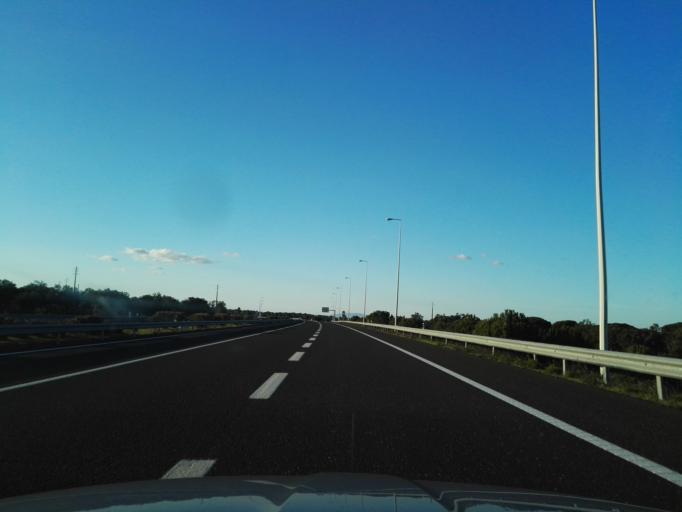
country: PT
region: Santarem
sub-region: Benavente
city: Poceirao
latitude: 38.8340
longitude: -8.7224
